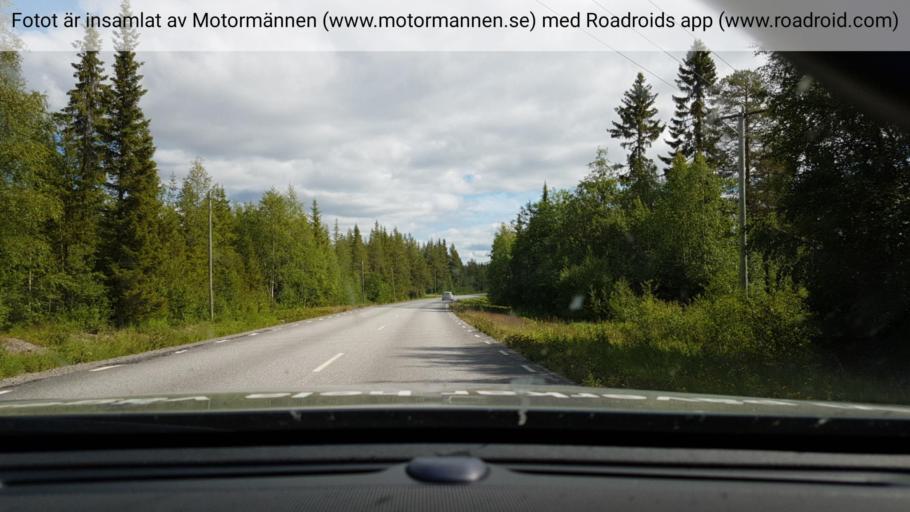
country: SE
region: Vaesterbotten
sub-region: Sorsele Kommun
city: Sorsele
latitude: 65.6563
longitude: 17.4320
